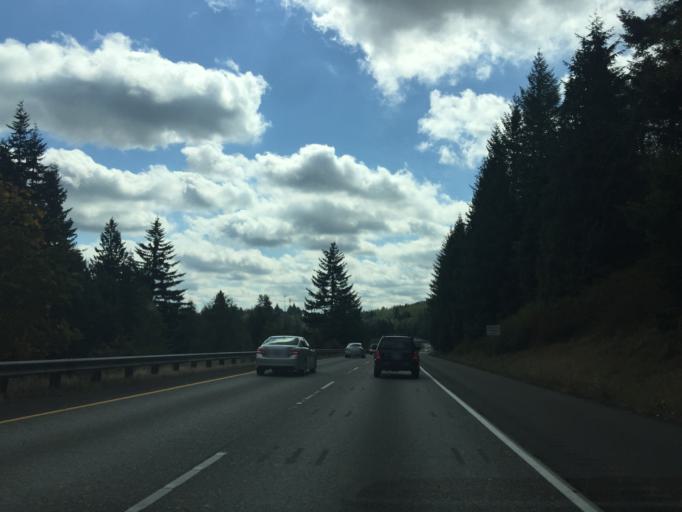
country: US
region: Washington
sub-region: Whatcom County
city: Sudden Valley
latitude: 48.6278
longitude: -122.3577
